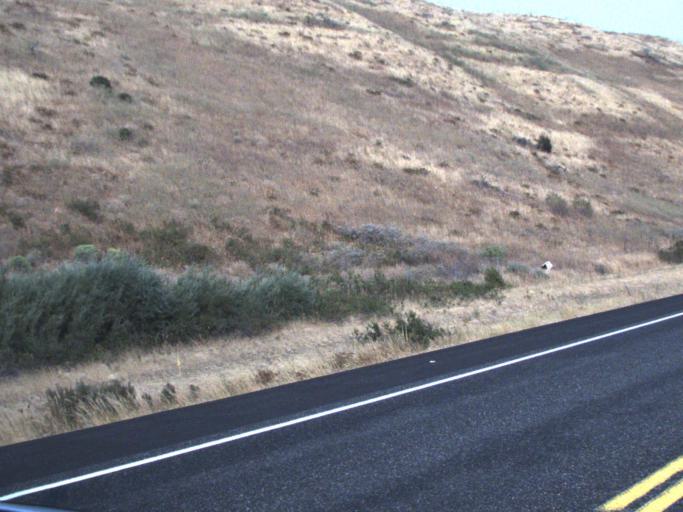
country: US
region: Washington
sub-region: Kittitas County
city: Ellensburg
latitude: 47.0908
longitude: -120.6538
